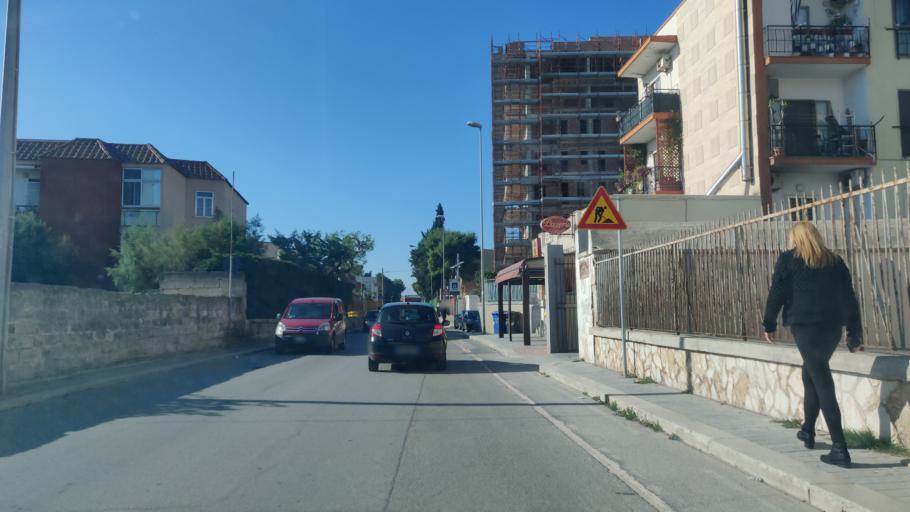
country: IT
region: Apulia
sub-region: Provincia di Bari
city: San Paolo
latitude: 41.1359
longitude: 16.8226
